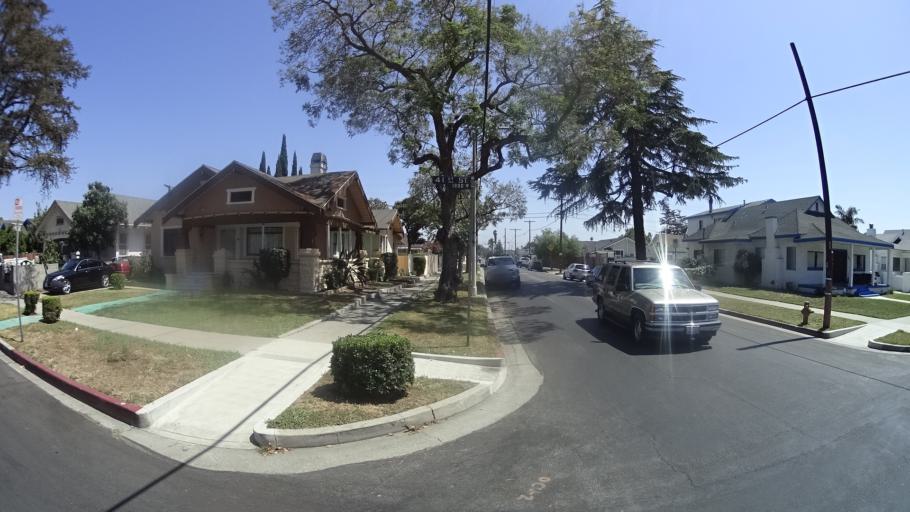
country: US
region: California
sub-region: Los Angeles County
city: View Park-Windsor Hills
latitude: 34.0099
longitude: -118.3138
